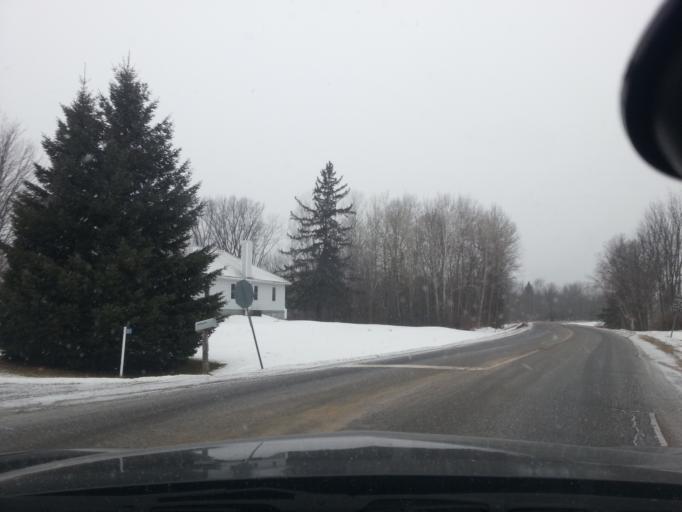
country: CA
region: Ontario
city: Arnprior
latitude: 45.3174
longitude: -76.3042
